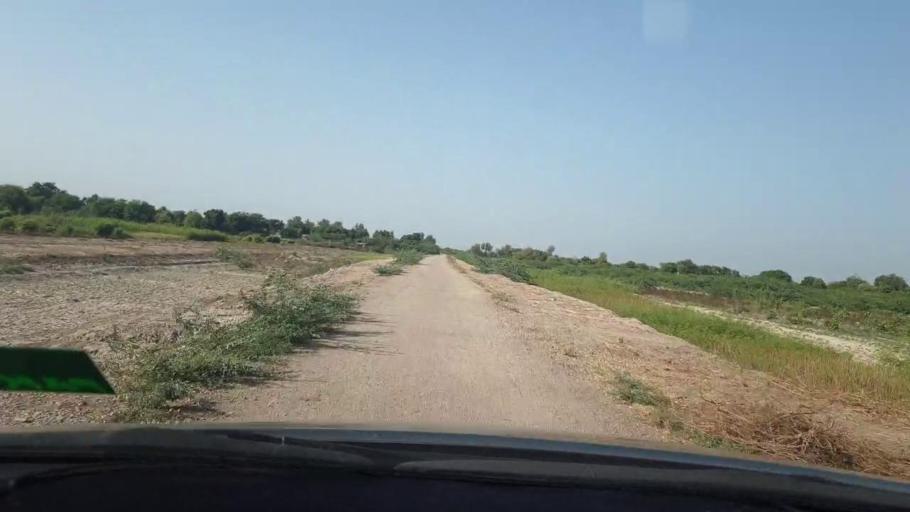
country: PK
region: Sindh
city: Naukot
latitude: 24.8649
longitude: 69.3181
